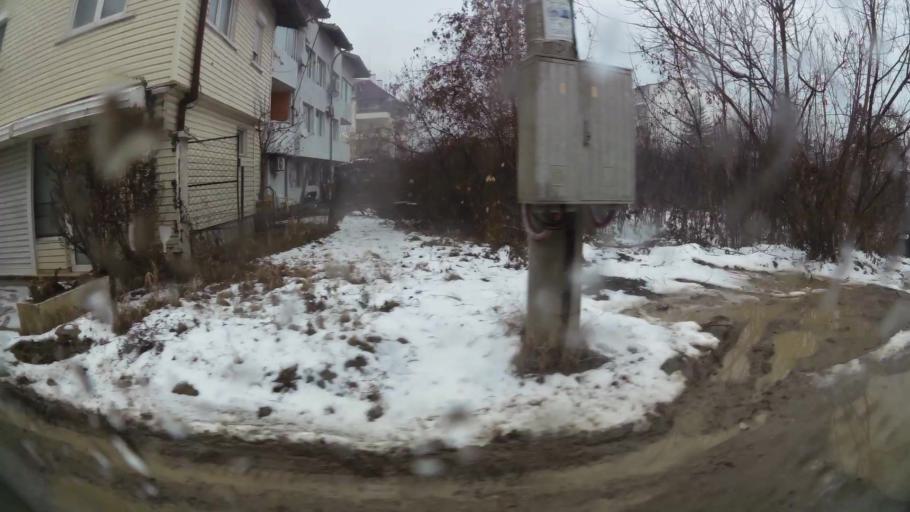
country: BG
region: Sofia-Capital
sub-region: Stolichna Obshtina
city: Sofia
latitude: 42.6796
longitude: 23.2591
